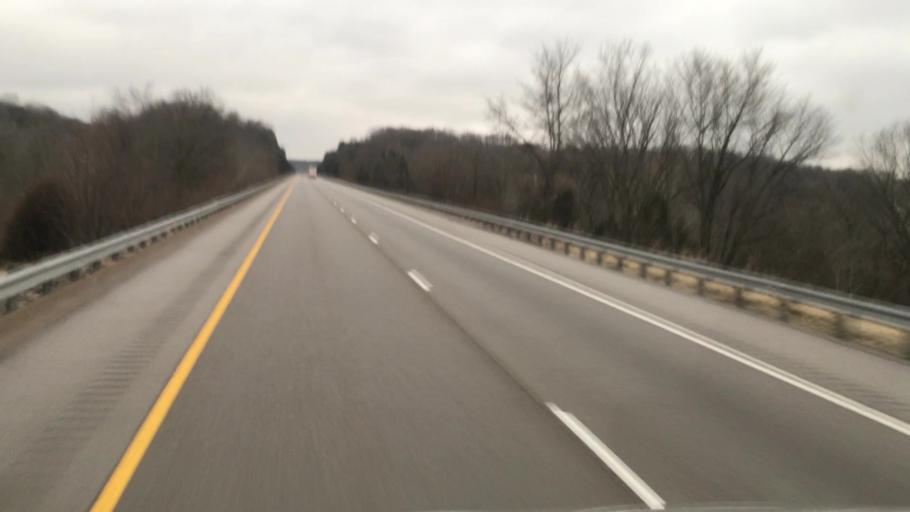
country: US
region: Illinois
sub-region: Johnson County
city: Vienna
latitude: 37.4752
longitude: -88.8917
